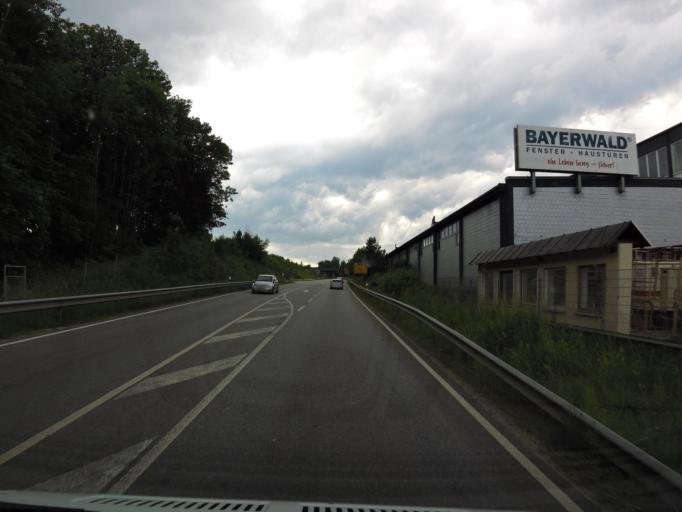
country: DE
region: Bavaria
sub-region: Lower Bavaria
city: Neukirchen vorm Wald
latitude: 48.6942
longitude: 13.3919
